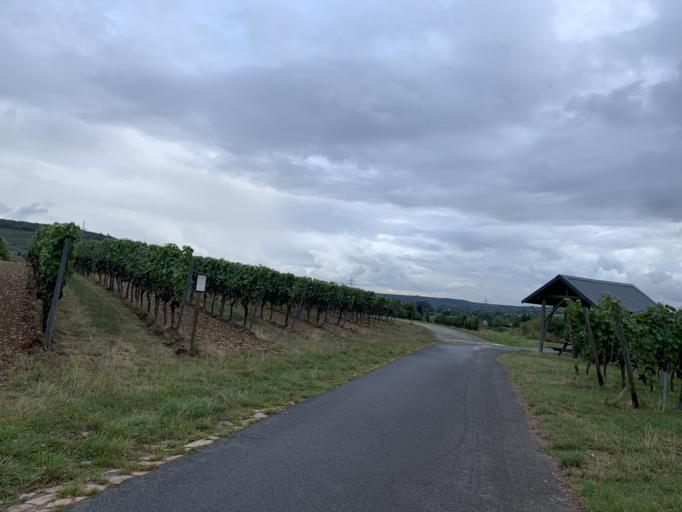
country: DE
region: Rheinland-Pfalz
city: Windesheim
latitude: 49.9119
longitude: 7.8143
